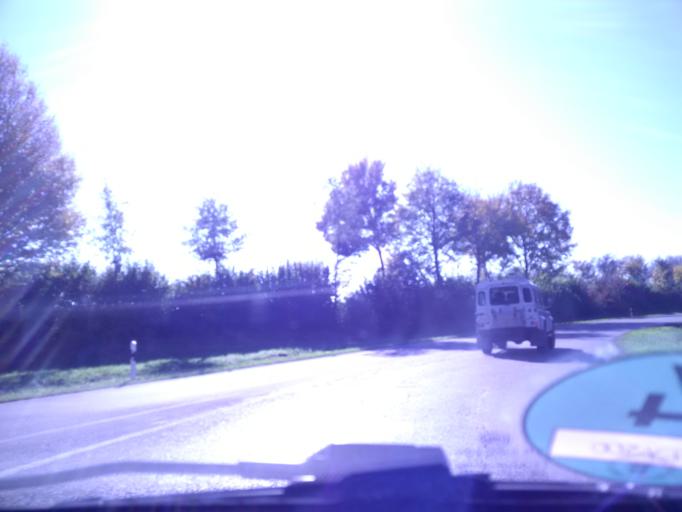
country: DE
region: Baden-Wuerttemberg
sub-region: Tuebingen Region
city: Huttisheim
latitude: 48.3295
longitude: 9.9428
